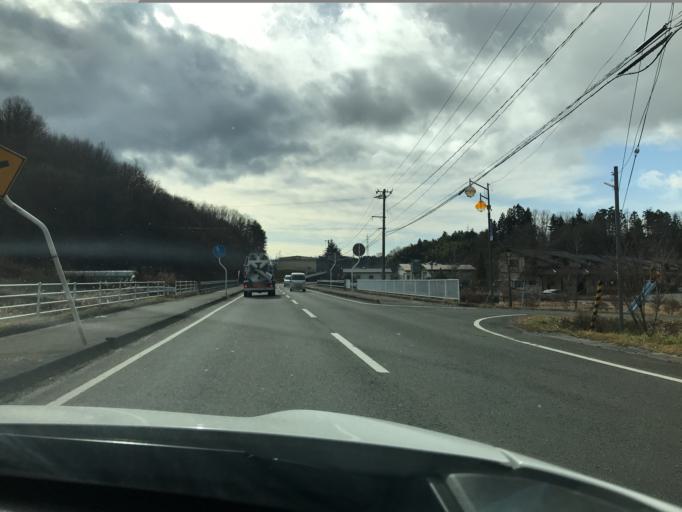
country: JP
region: Fukushima
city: Funehikimachi-funehiki
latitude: 37.5729
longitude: 140.5789
